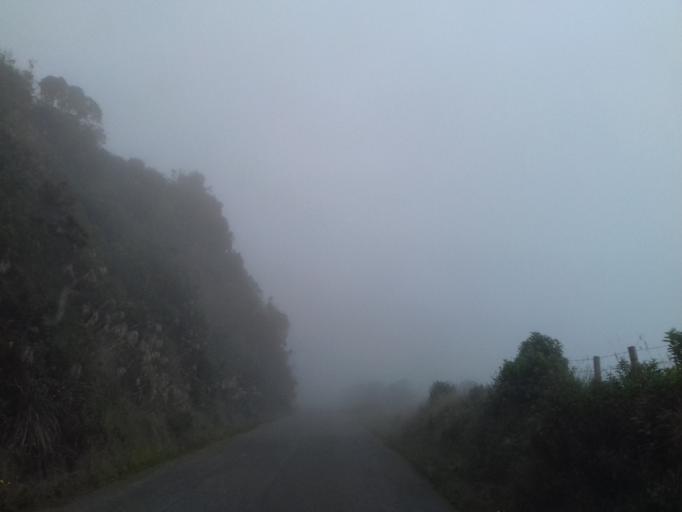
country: CO
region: Tolima
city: Herveo
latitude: 5.0057
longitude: -75.3270
